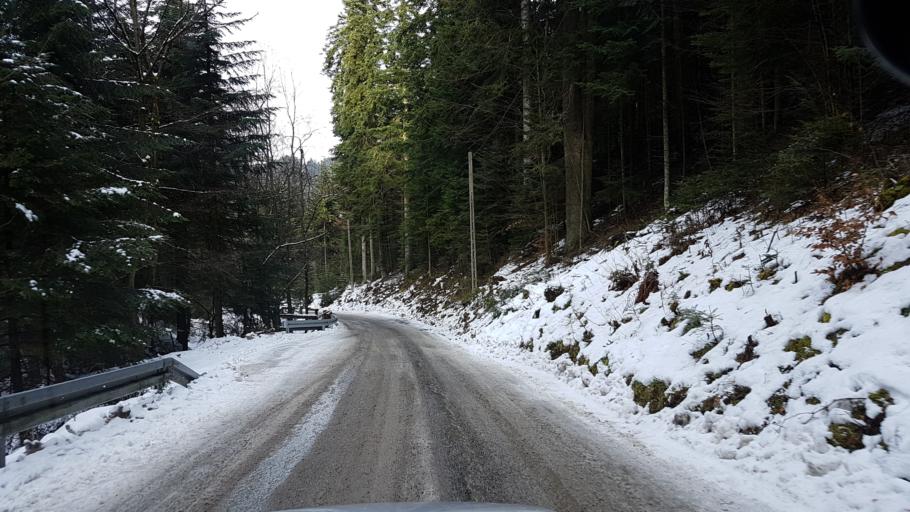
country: PL
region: Lesser Poland Voivodeship
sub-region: Powiat nowosadecki
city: Piwniczna-Zdroj
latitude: 49.4172
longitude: 20.6452
